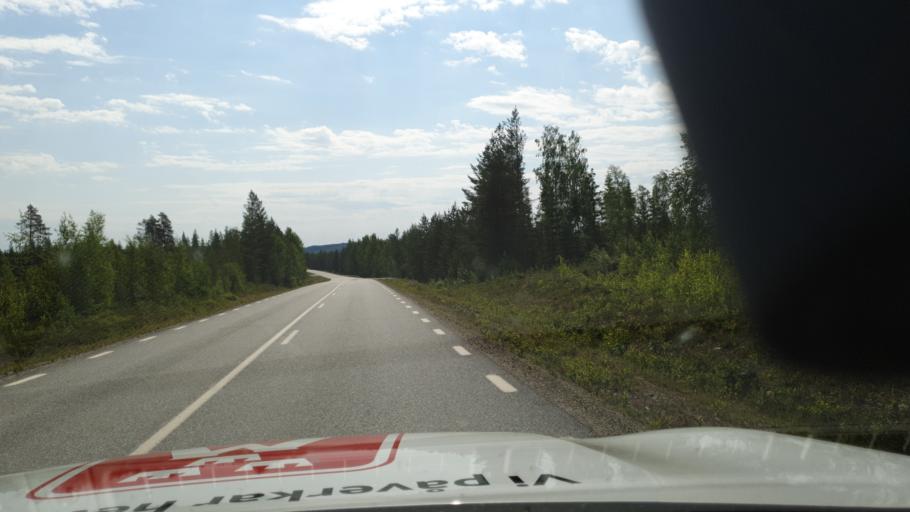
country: SE
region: Vaesterbotten
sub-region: Vindelns Kommun
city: Vindeln
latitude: 64.3320
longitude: 19.5126
